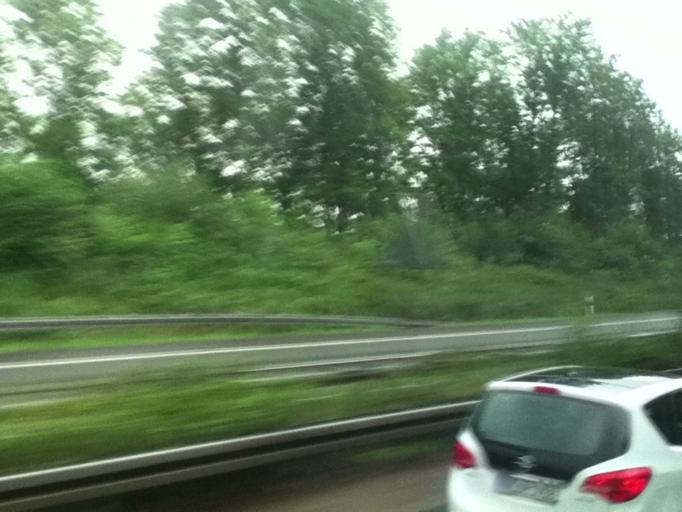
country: DE
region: North Rhine-Westphalia
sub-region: Regierungsbezirk Koln
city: Engelskirchen
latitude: 50.9792
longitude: 7.4187
